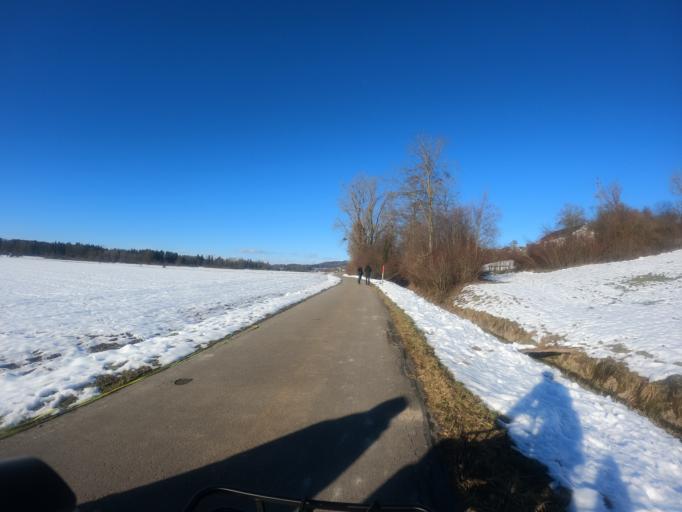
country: CH
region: Aargau
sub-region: Bezirk Bremgarten
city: Oberlunkhofen
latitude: 47.3055
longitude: 8.3870
